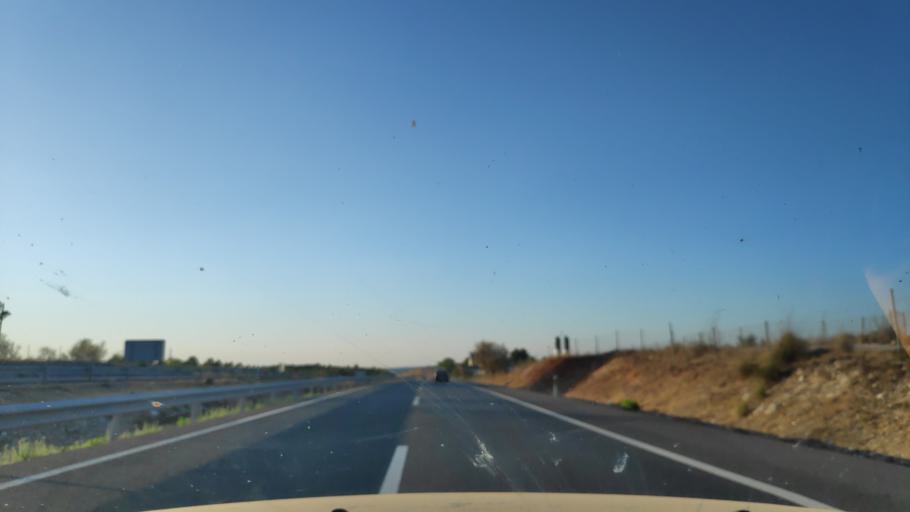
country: ES
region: Madrid
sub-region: Provincia de Madrid
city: Villarejo de Salvanes
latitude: 40.1815
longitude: -3.2969
